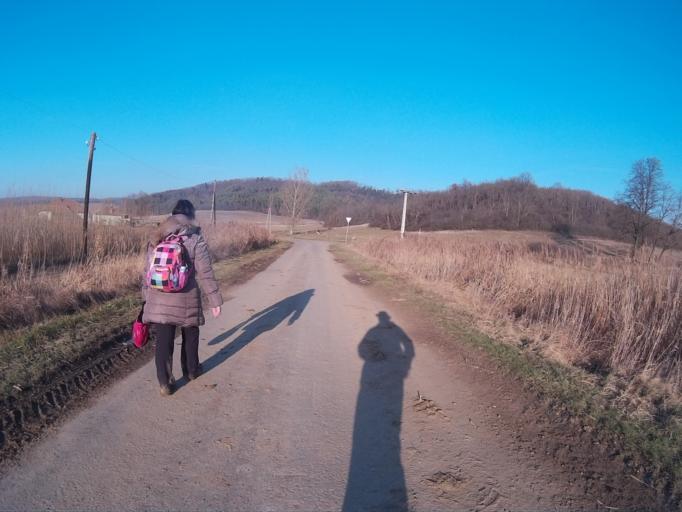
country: HU
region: Nograd
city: Bercel
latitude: 47.9755
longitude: 19.4363
